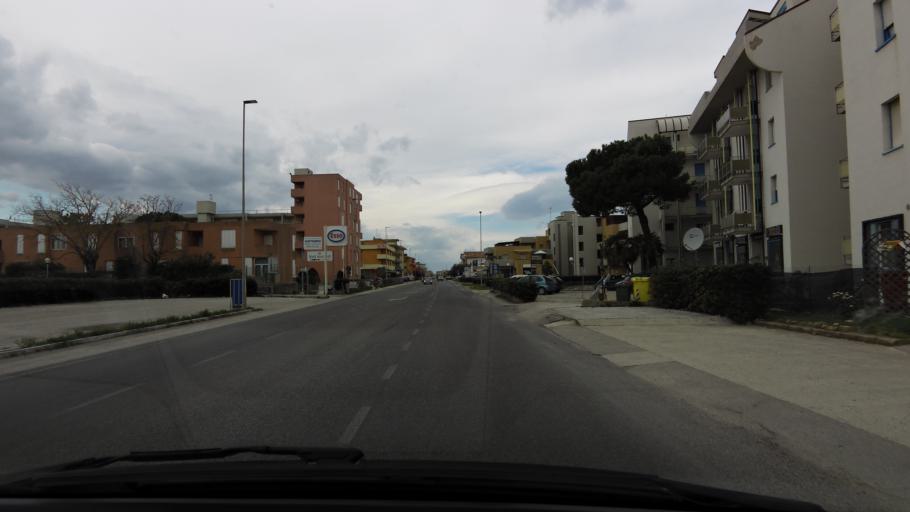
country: IT
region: The Marches
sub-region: Provincia di Pesaro e Urbino
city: Marotta
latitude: 43.7634
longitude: 13.1471
